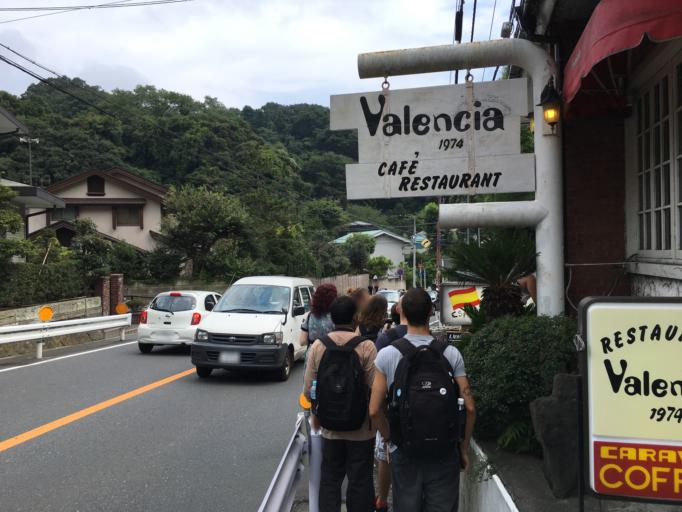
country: JP
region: Kanagawa
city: Kamakura
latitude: 35.3281
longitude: 139.5558
